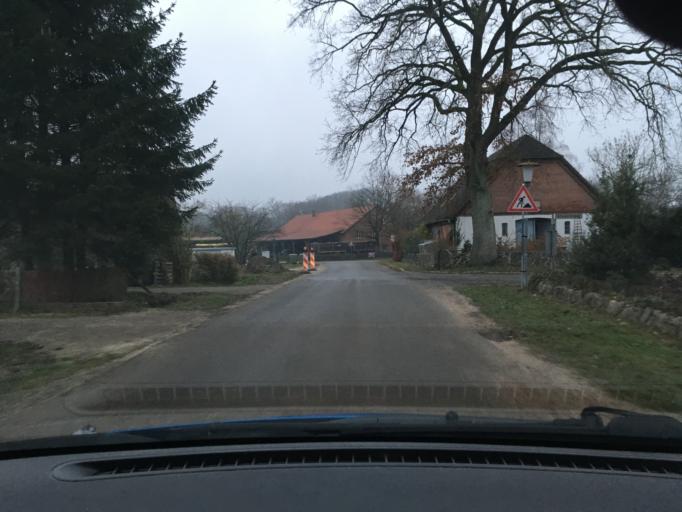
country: DE
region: Lower Saxony
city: Soderstorf
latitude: 53.1615
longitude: 10.1603
